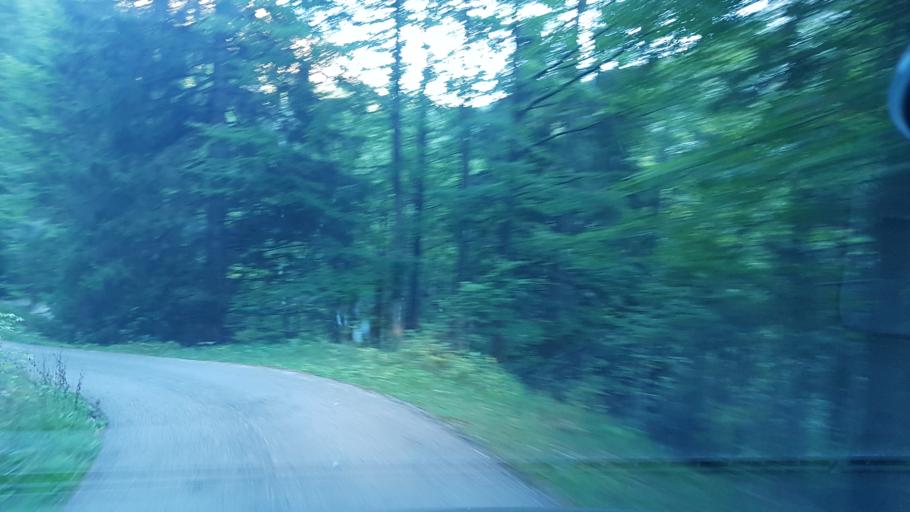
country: IT
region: Veneto
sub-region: Provincia di Belluno
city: Fusine
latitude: 46.3492
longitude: 12.0930
